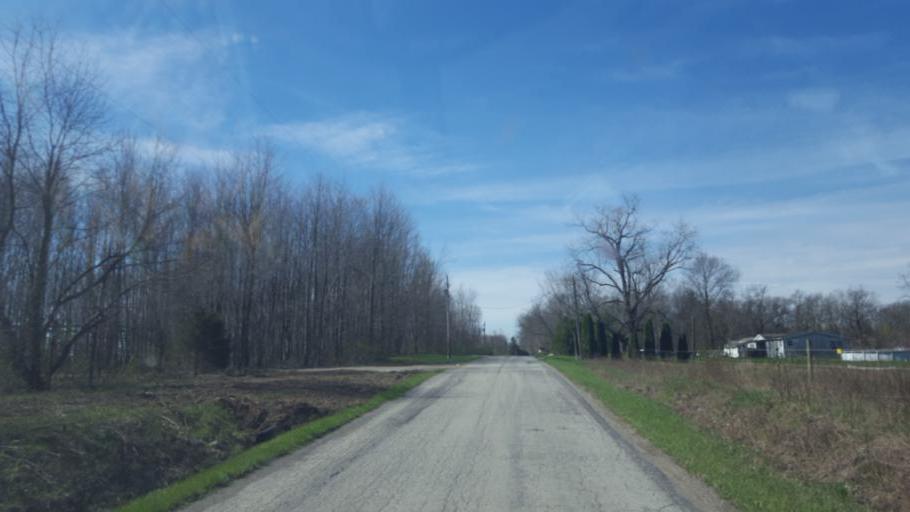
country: US
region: Ohio
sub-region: Delaware County
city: Ashley
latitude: 40.4501
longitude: -82.9589
